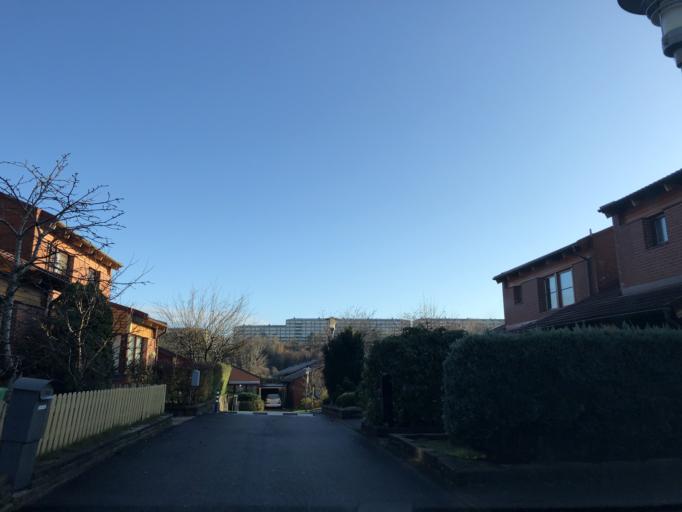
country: SE
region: Vaestra Goetaland
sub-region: Goteborg
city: Rannebergen
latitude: 57.8006
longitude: 12.0604
